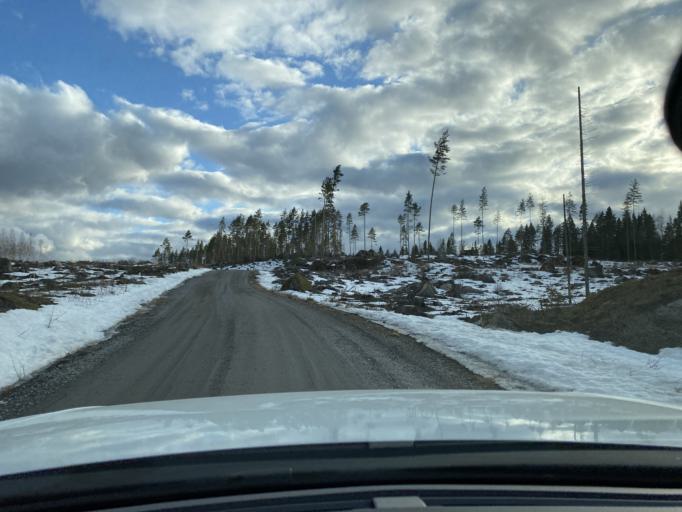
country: FI
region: Pirkanmaa
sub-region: Lounais-Pirkanmaa
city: Mouhijaervi
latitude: 61.4370
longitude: 22.9660
